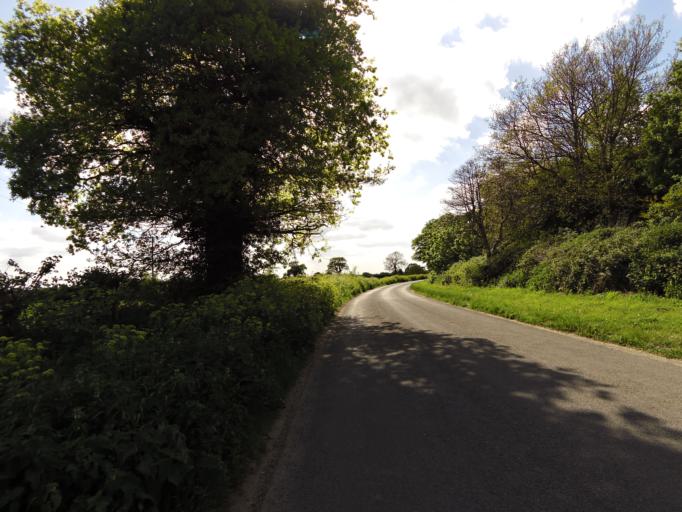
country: GB
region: England
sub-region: Suffolk
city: Kessingland
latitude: 52.4394
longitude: 1.6668
